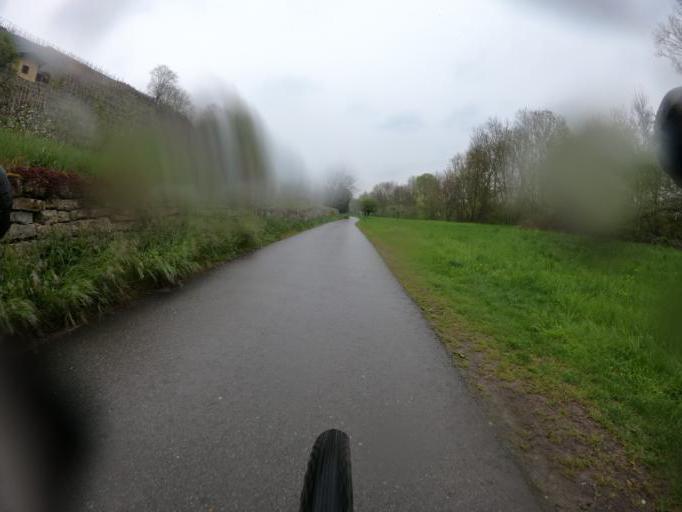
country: DE
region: Baden-Wuerttemberg
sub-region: Regierungsbezirk Stuttgart
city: Vaihingen an der Enz
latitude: 48.9220
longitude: 8.9856
